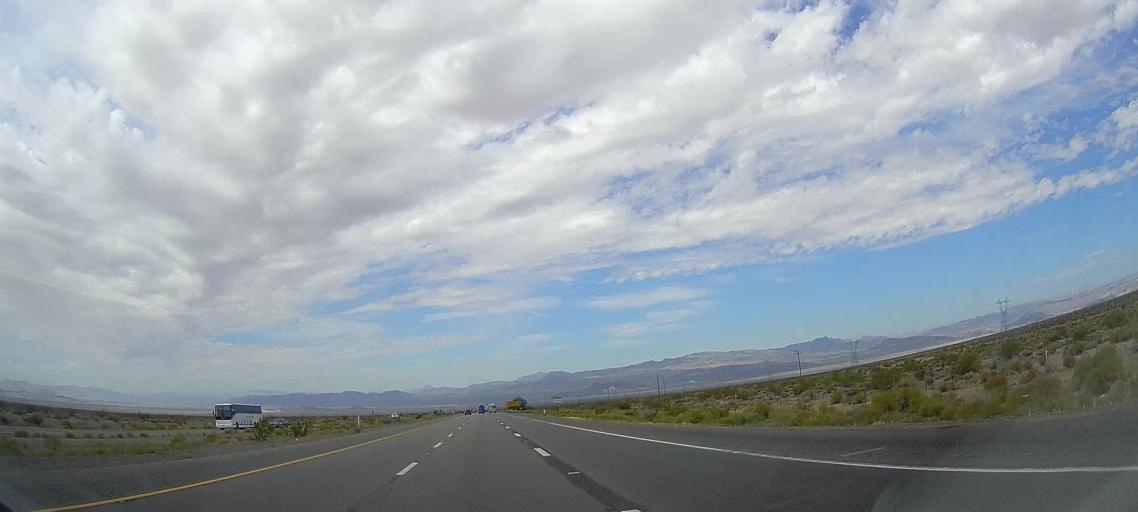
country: US
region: Nevada
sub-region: Clark County
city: Sandy Valley
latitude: 35.3310
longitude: -115.9716
